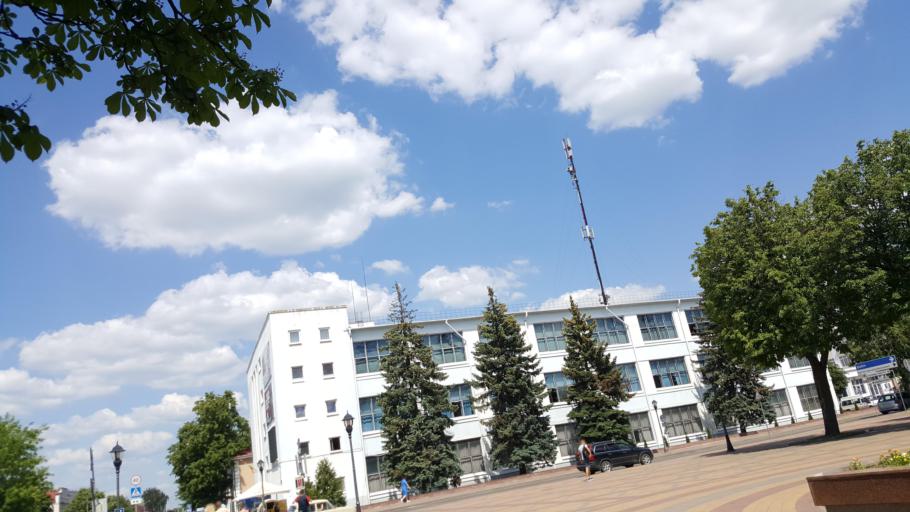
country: BY
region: Brest
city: Kobryn
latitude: 52.2114
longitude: 24.3562
